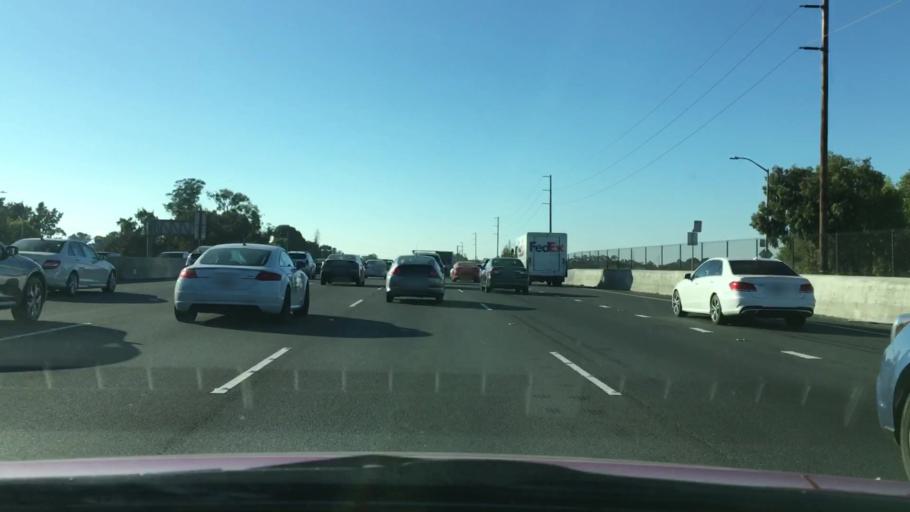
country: US
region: California
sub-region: Santa Clara County
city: Palo Alto
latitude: 37.4401
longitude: -122.1123
